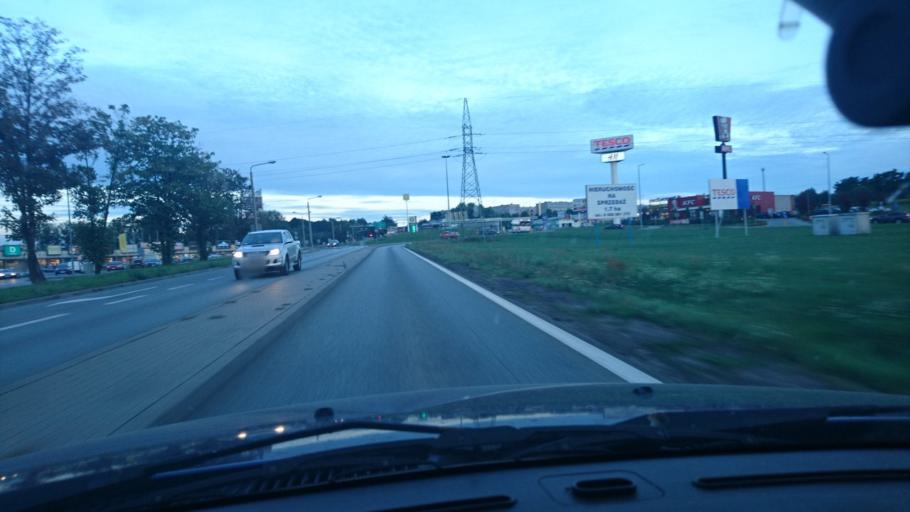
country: PL
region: Silesian Voivodeship
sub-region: Powiat tarnogorski
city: Tarnowskie Gory
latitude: 50.4553
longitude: 18.8350
